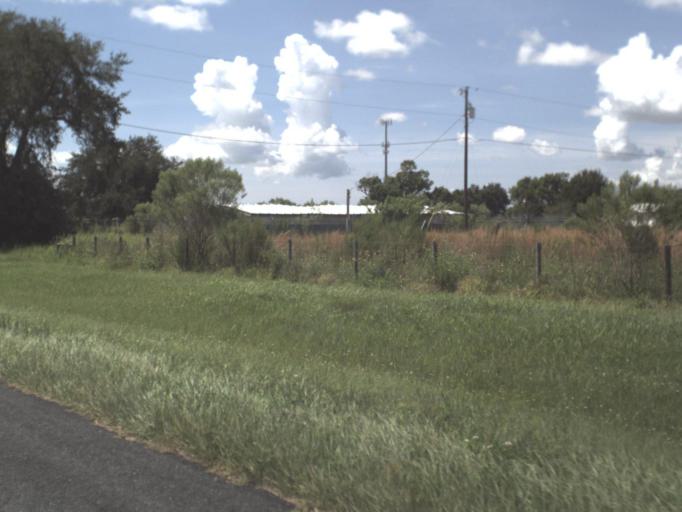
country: US
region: Florida
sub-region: Charlotte County
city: Harbour Heights
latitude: 27.0720
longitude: -81.9584
